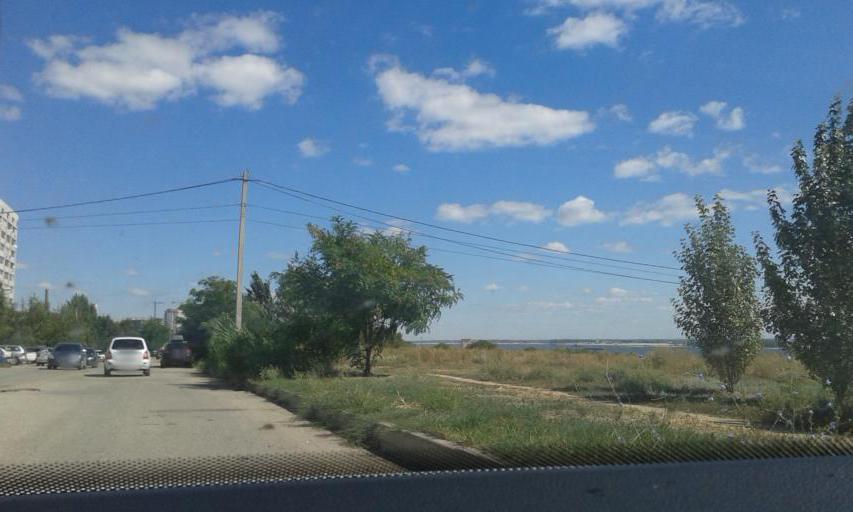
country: RU
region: Volgograd
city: Volgograd
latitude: 48.6752
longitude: 44.4782
